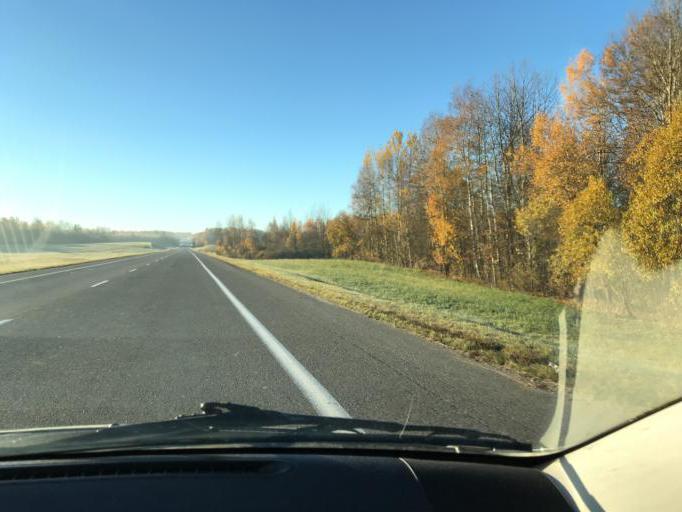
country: BY
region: Vitebsk
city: Vitebsk
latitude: 55.0727
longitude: 30.3082
